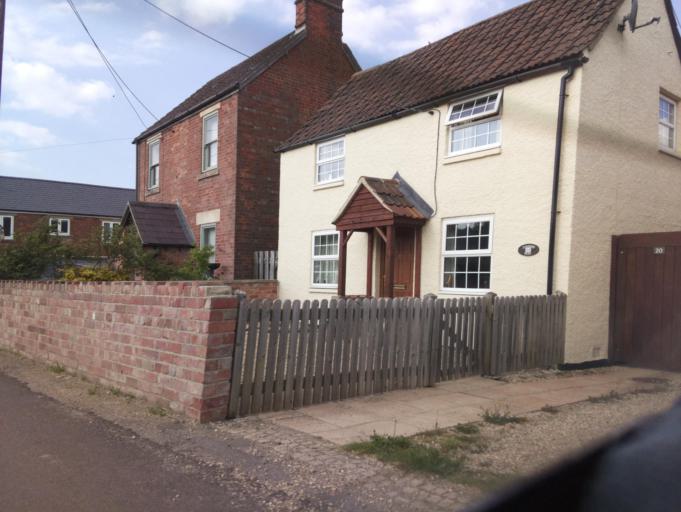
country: GB
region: England
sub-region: Wiltshire
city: Malmesbury
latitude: 51.5249
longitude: -2.0776
